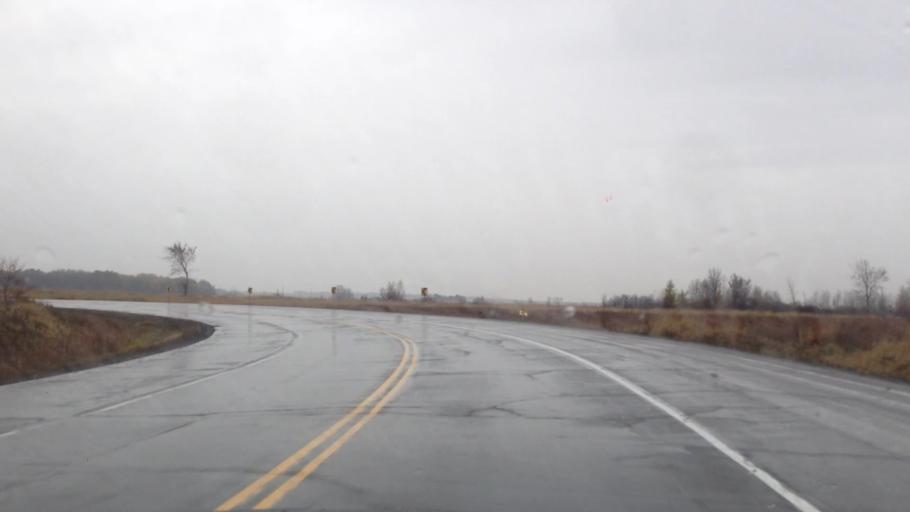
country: CA
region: Ontario
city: Clarence-Rockland
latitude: 45.4726
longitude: -75.4411
